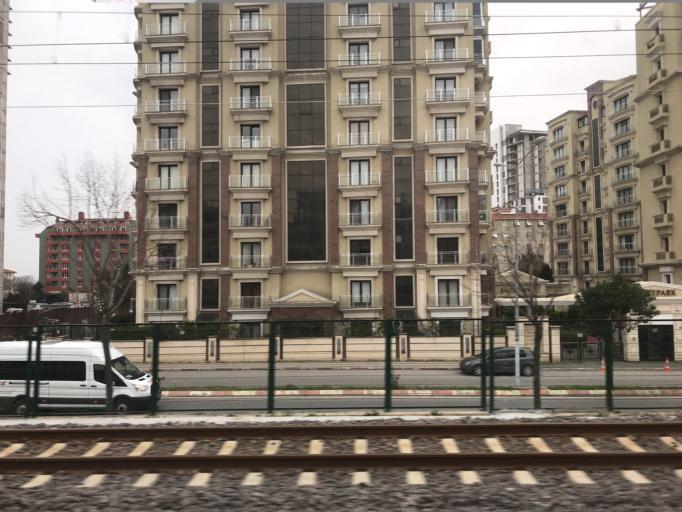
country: TR
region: Istanbul
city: Maltepe
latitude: 40.9020
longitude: 29.1655
